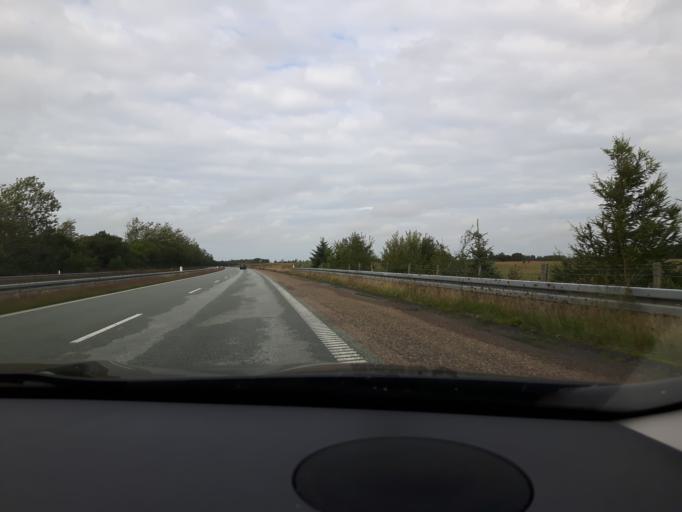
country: DK
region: North Denmark
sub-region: Hjorring Kommune
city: Hjorring
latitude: 57.4889
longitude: 10.0265
